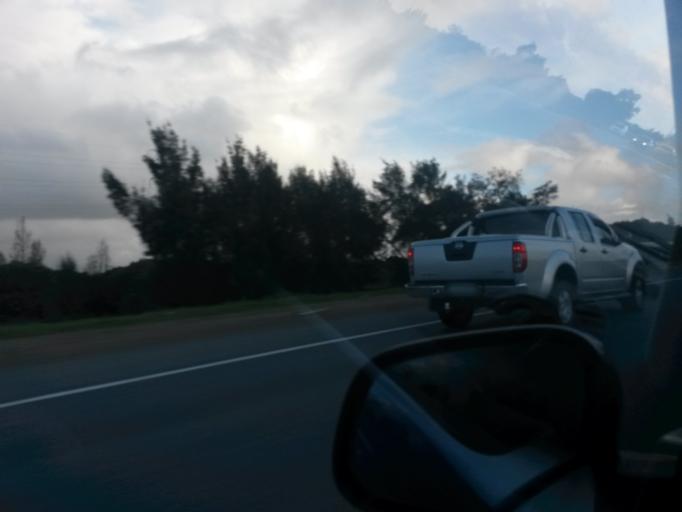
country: AU
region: South Australia
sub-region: Port Adelaide Enfield
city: Enfield
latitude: -34.8305
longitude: 138.5844
